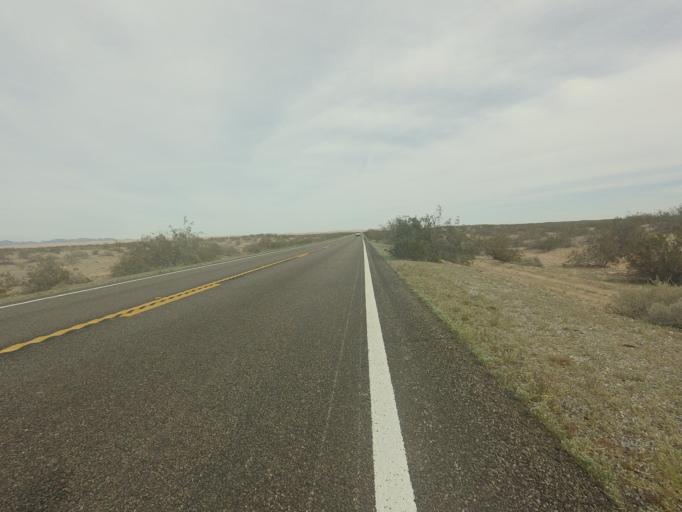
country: US
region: California
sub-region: Imperial County
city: Holtville
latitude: 32.9705
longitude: -115.2493
